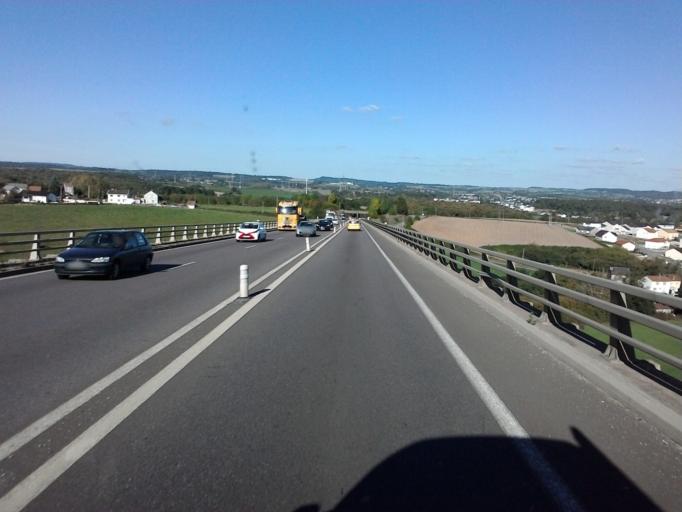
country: FR
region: Lorraine
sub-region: Departement de Meurthe-et-Moselle
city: Longwy
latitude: 49.5448
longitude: 5.7679
